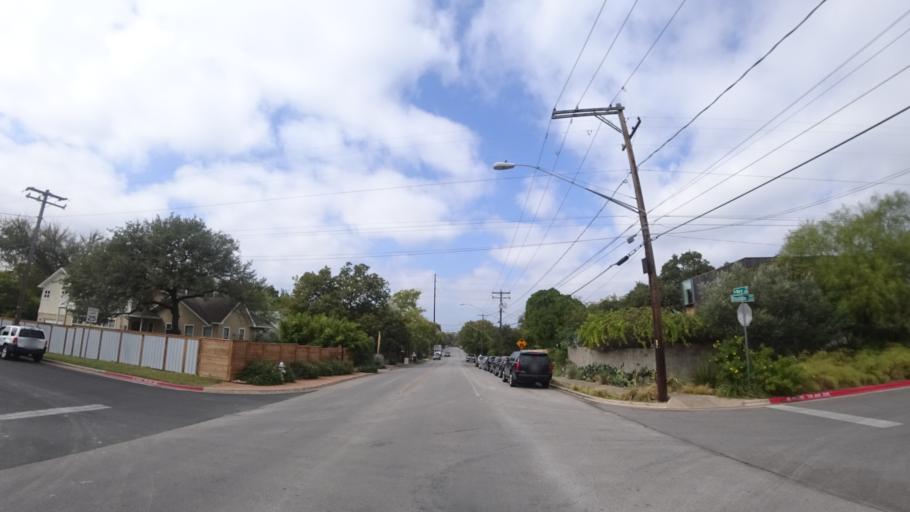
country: US
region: Texas
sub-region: Travis County
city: Austin
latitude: 30.2478
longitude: -97.7606
